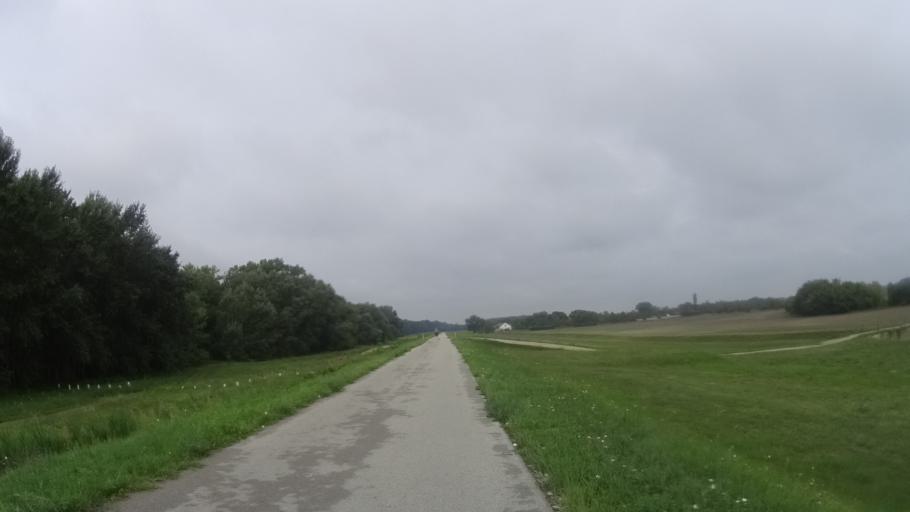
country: SK
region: Nitriansky
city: Komarno
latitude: 47.7471
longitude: 18.1655
